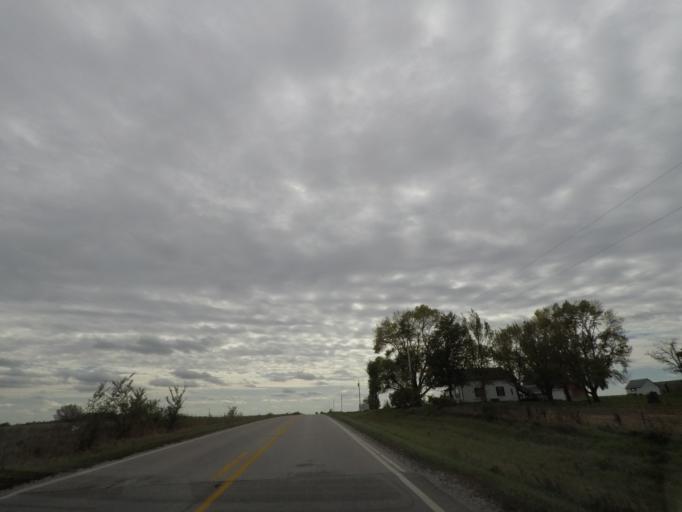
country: US
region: Iowa
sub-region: Story County
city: Huxley
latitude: 41.8627
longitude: -93.5317
